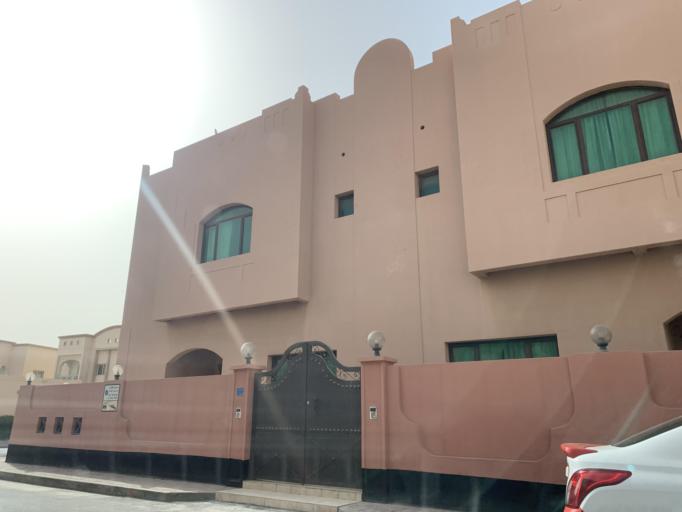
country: BH
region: Manama
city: Manama
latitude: 26.2097
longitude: 50.6145
